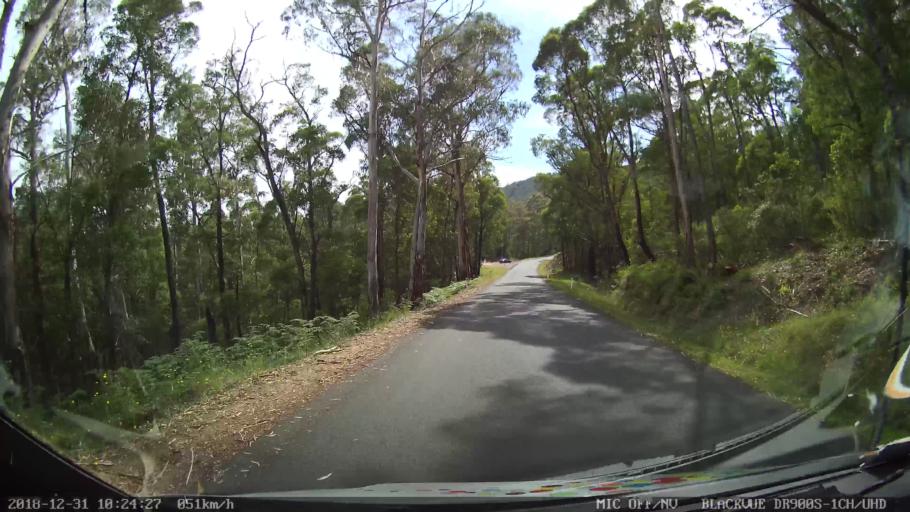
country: AU
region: New South Wales
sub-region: Snowy River
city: Jindabyne
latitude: -36.5122
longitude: 148.1402
